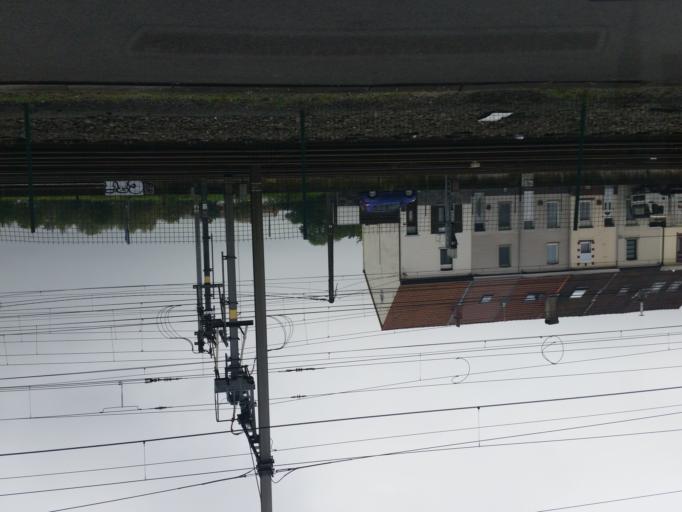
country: BE
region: Flanders
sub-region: Provincie Vlaams-Brabant
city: Drogenbos
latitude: 50.7943
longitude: 4.2980
